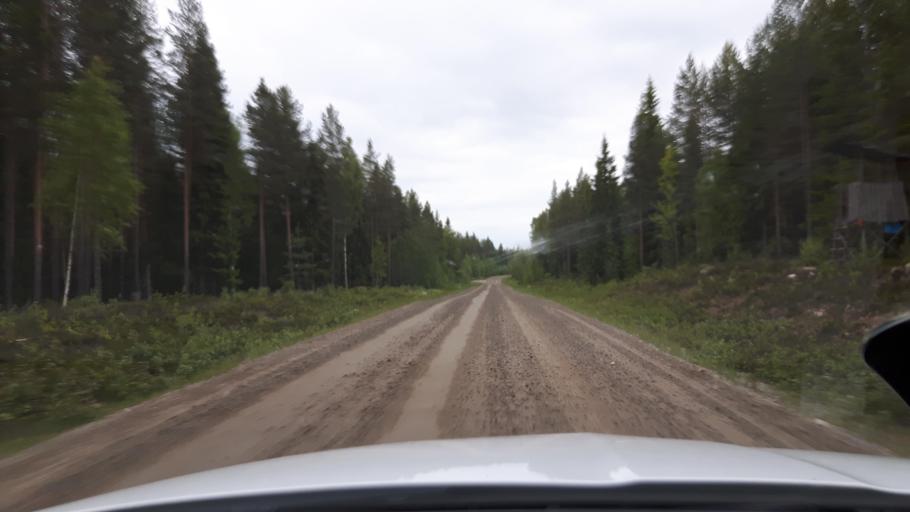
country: SE
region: Gaevleborg
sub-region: Ljusdals Kommun
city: Farila
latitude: 62.0178
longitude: 15.8369
